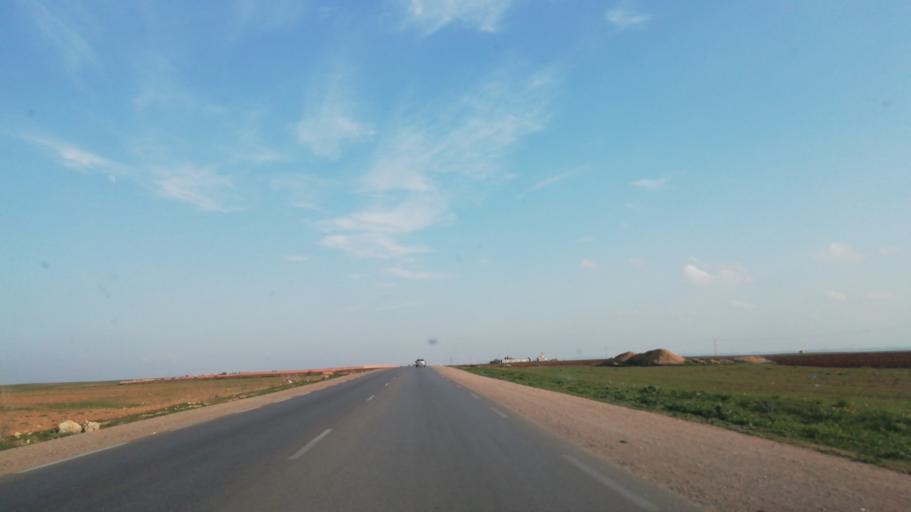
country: DZ
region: Relizane
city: Relizane
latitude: 35.8944
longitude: 0.6069
